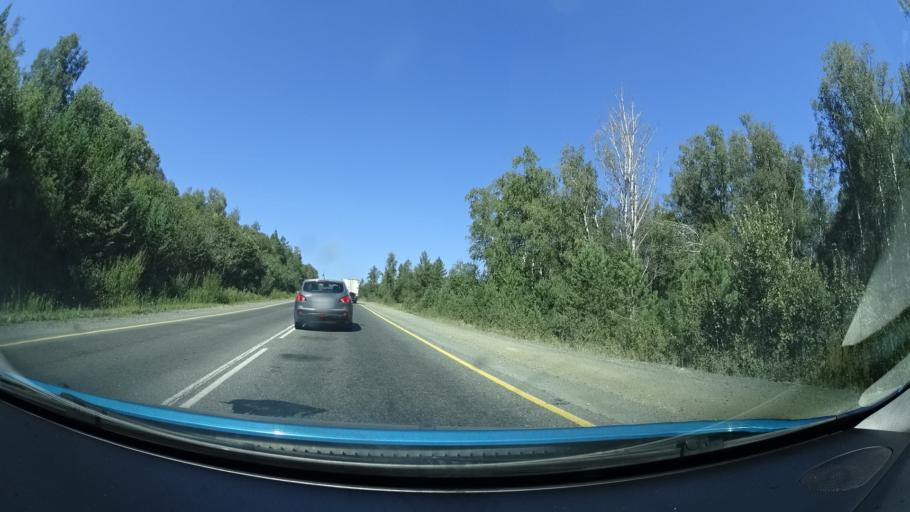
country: RU
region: Bashkortostan
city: Abzakovo
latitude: 53.8900
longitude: 58.5220
